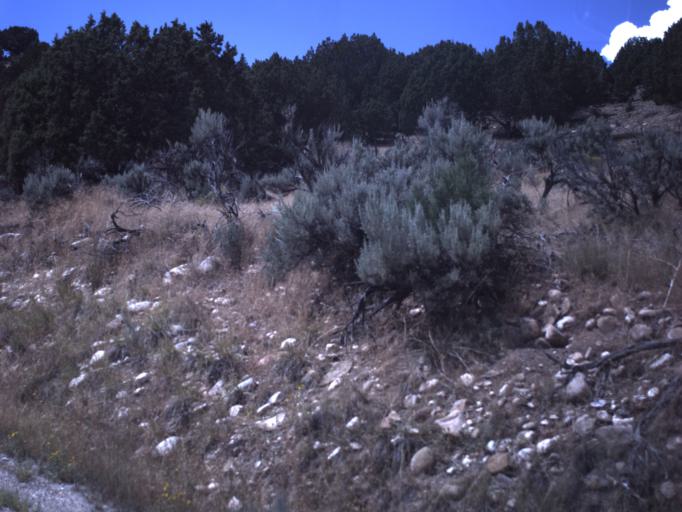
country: US
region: Utah
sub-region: Summit County
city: Oakley
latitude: 40.7664
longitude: -111.3823
